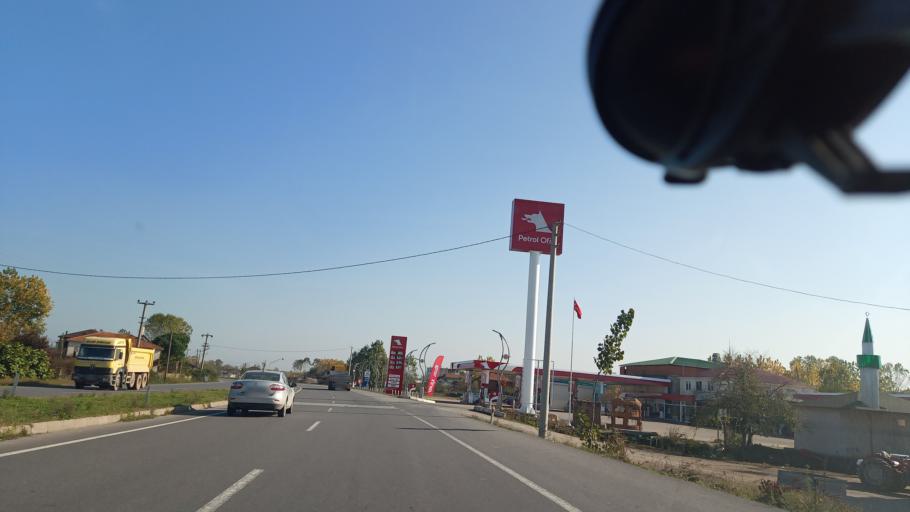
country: TR
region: Sakarya
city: Karasu
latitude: 41.0697
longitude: 30.7984
